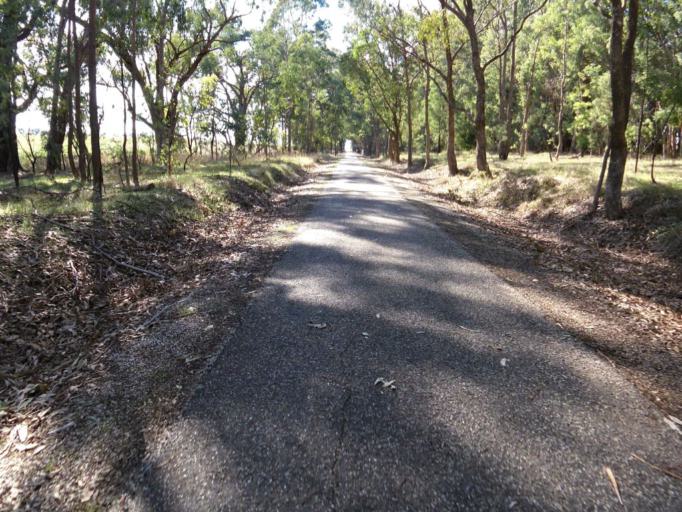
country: AU
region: Victoria
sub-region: Wangaratta
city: Wangaratta
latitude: -36.4007
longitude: 146.6453
